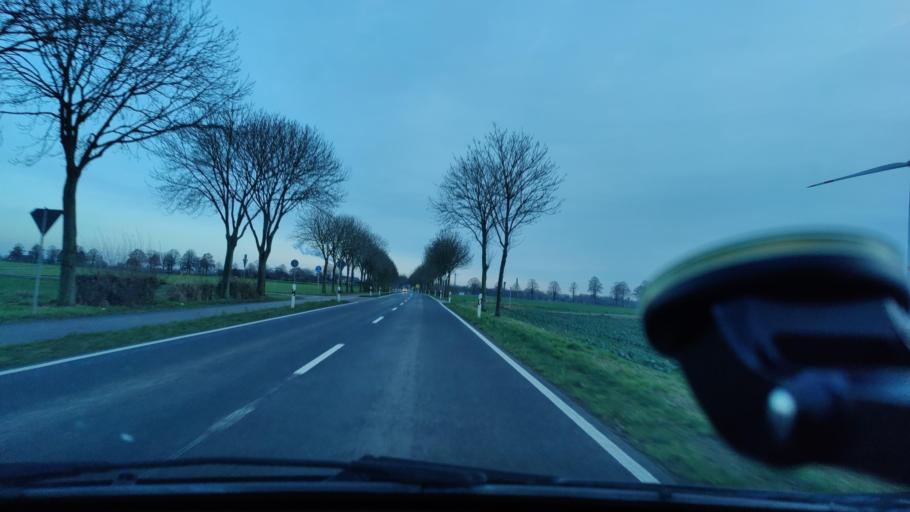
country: DE
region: North Rhine-Westphalia
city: Kalkar
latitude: 51.7463
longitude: 6.3231
